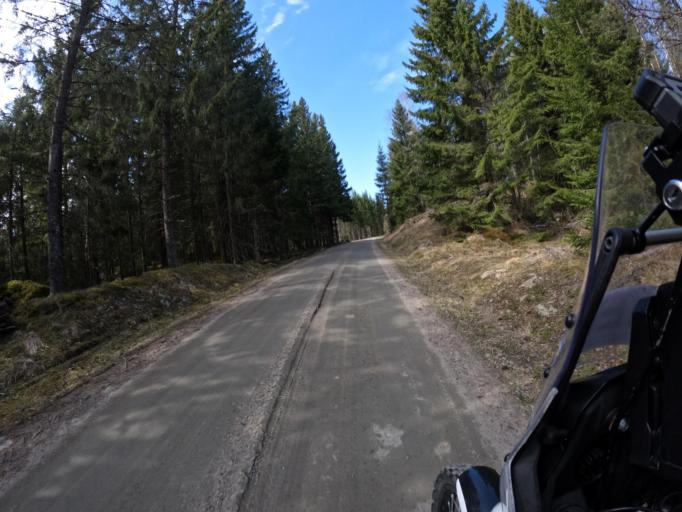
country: SE
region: Vaestra Goetaland
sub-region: Ulricehamns Kommun
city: Ulricehamn
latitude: 57.9328
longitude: 13.6037
